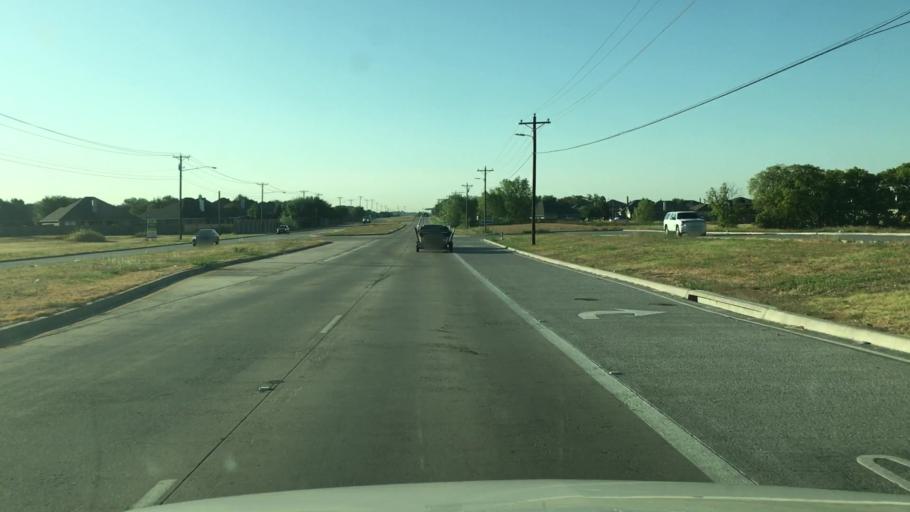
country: US
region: Texas
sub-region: Johnson County
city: Burleson
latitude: 32.5377
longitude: -97.3594
